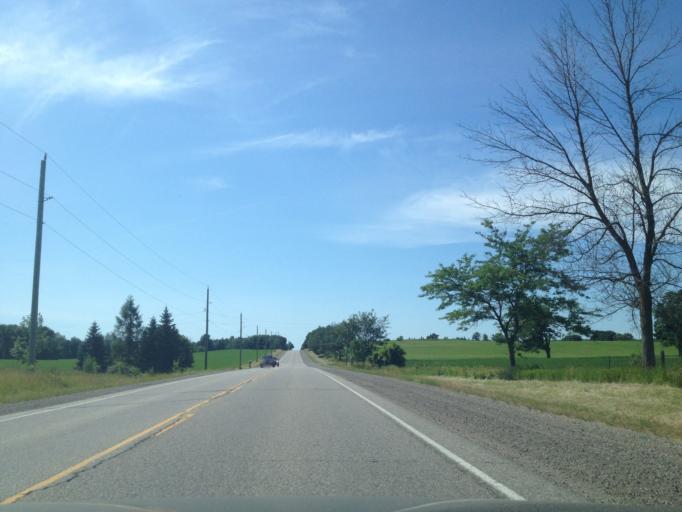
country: CA
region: Ontario
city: Stratford
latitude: 43.4701
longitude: -80.8006
